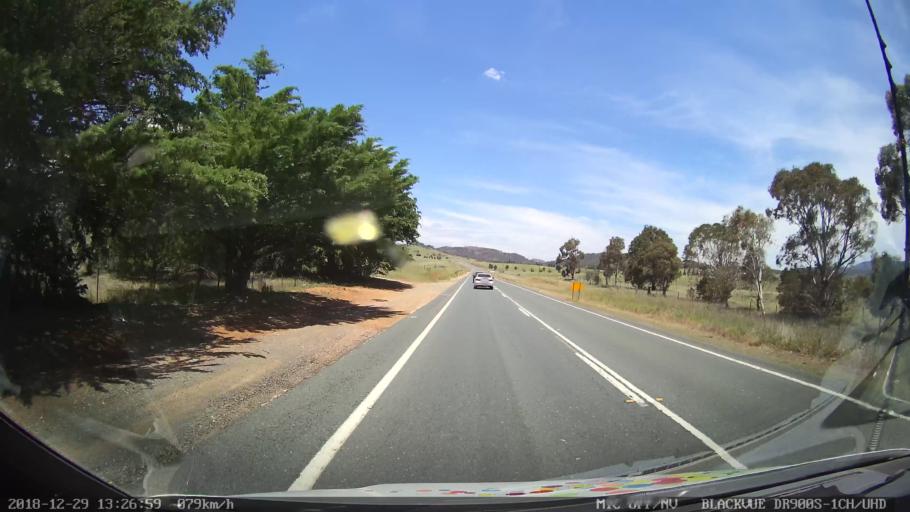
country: AU
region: New South Wales
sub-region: Cooma-Monaro
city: Cooma
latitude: -35.8617
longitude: 149.1583
